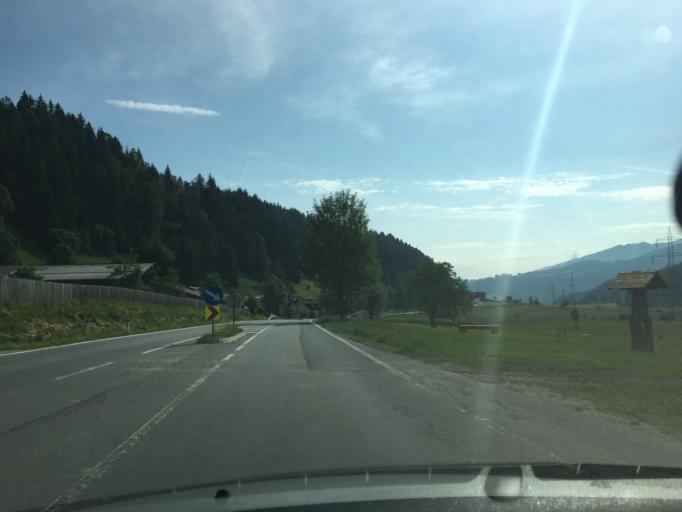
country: AT
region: Salzburg
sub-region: Politischer Bezirk Sankt Johann im Pongau
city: Wagrain
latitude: 47.3586
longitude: 13.3425
